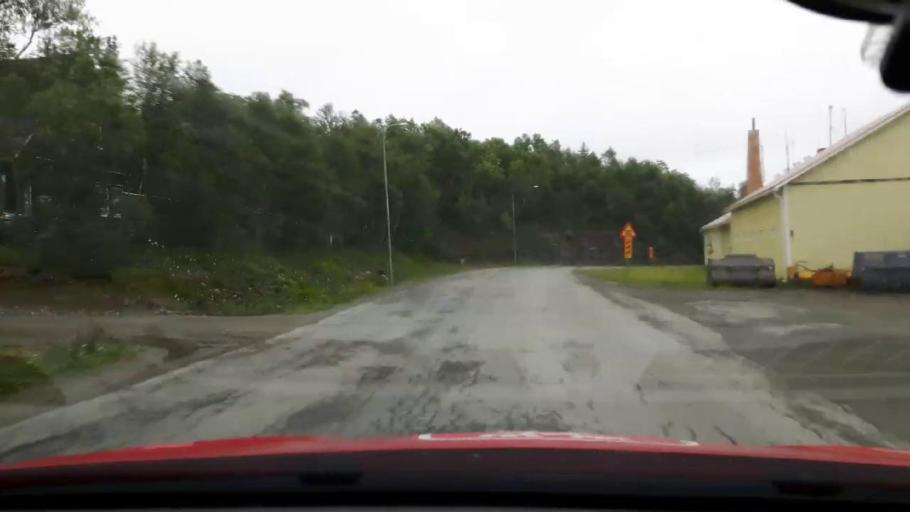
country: NO
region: Nord-Trondelag
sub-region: Meraker
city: Meraker
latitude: 63.3143
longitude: 12.1107
